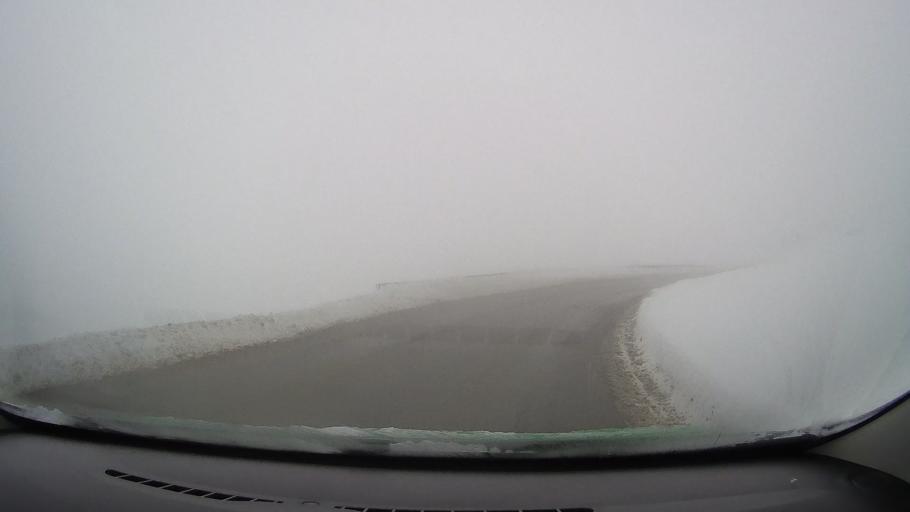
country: RO
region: Sibiu
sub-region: Comuna Poiana Sibiului
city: Poiana Sibiului
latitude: 45.7990
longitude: 23.7088
